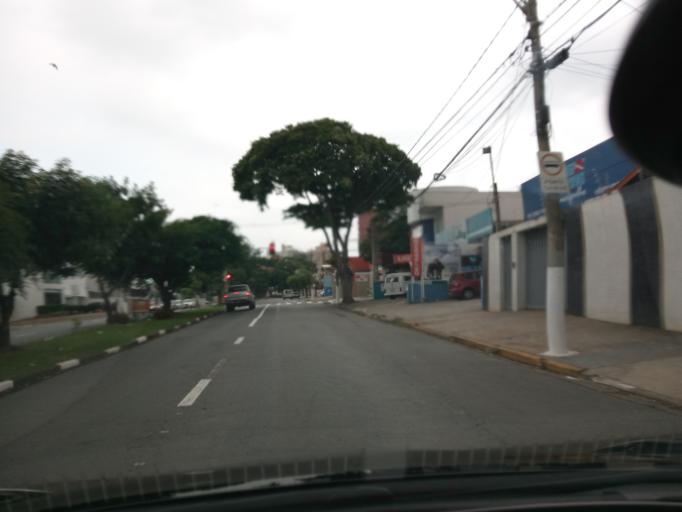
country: BR
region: Sao Paulo
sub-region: Campinas
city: Campinas
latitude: -22.8842
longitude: -47.0324
